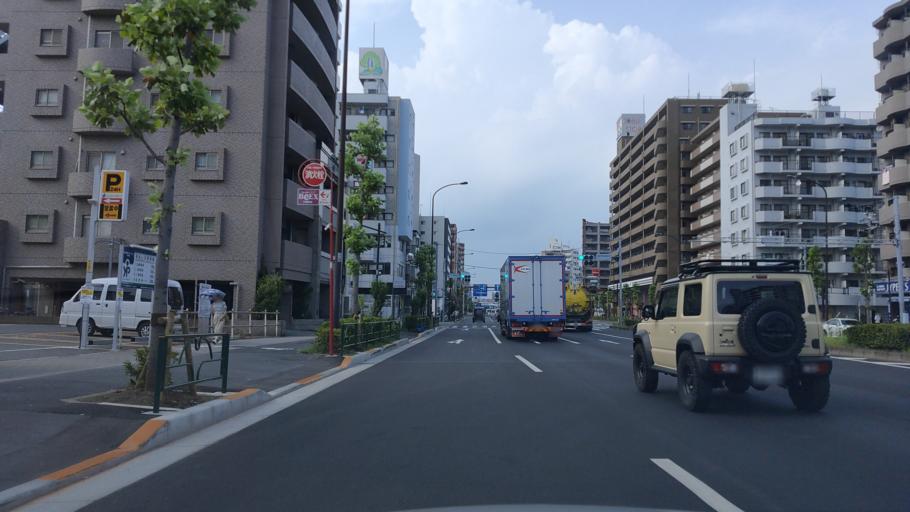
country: JP
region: Tokyo
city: Urayasu
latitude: 35.6537
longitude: 139.8723
